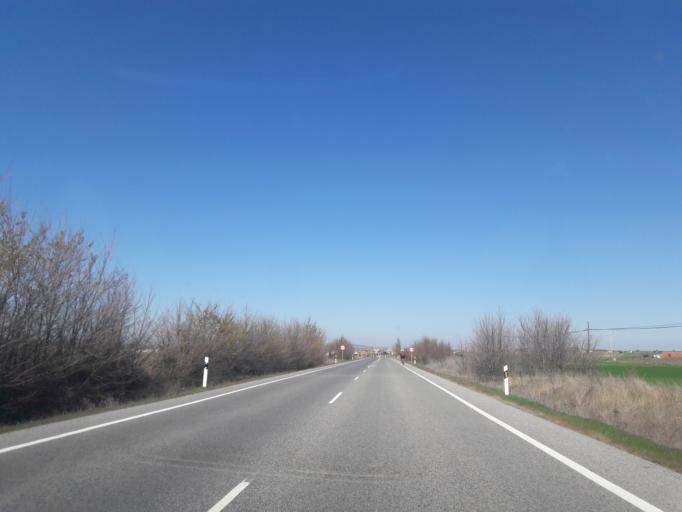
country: ES
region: Castille and Leon
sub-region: Provincia de Salamanca
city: Mozarbez
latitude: 40.8487
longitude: -5.6451
